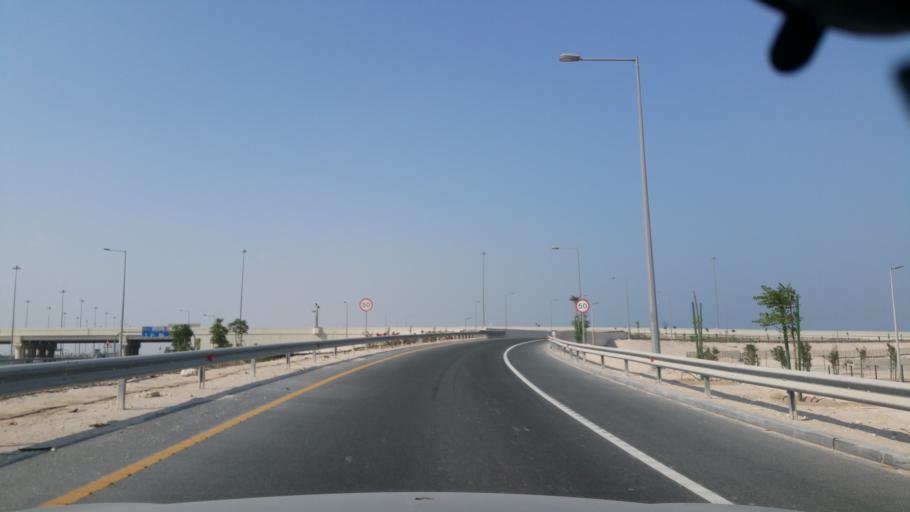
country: QA
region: Baladiyat Umm Salal
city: Umm Salal `Ali
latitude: 25.4540
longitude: 51.4792
